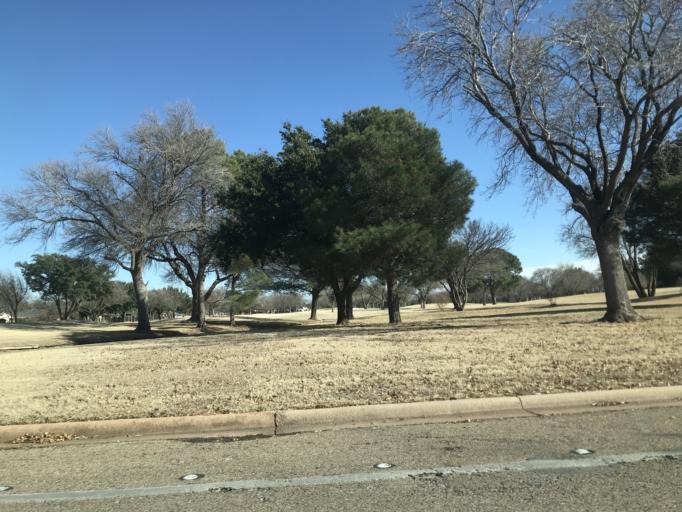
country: US
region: Texas
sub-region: Taylor County
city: Abilene
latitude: 32.3778
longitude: -99.7606
